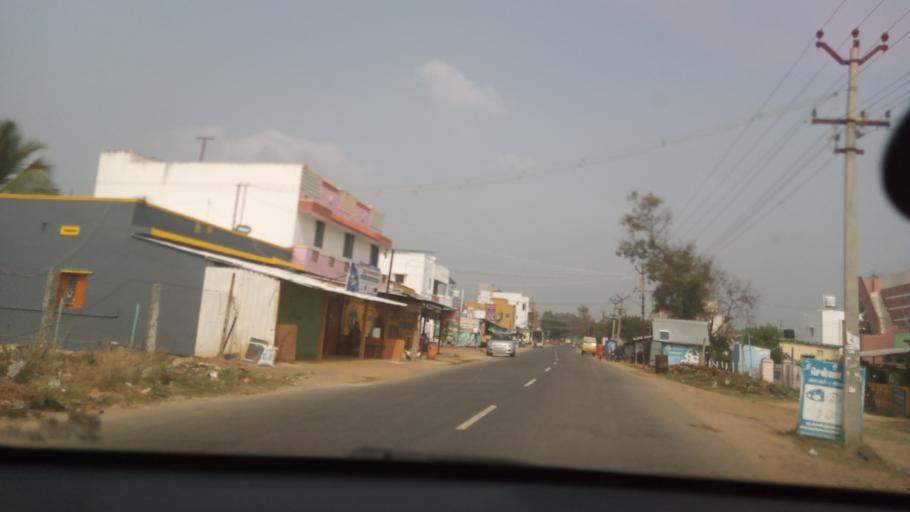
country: IN
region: Tamil Nadu
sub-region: Erode
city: Sathyamangalam
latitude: 11.5261
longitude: 77.1422
